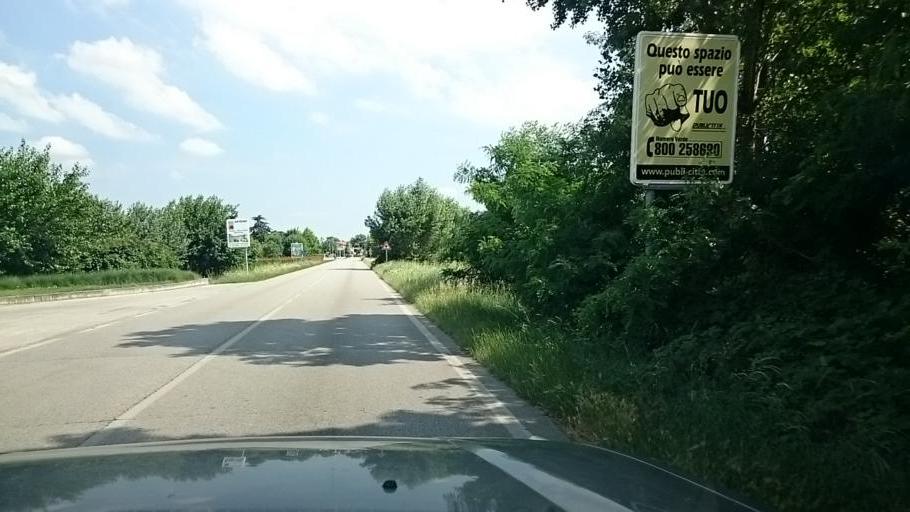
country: IT
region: Veneto
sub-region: Provincia di Vicenza
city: Cartigliano
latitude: 45.7202
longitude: 11.7028
